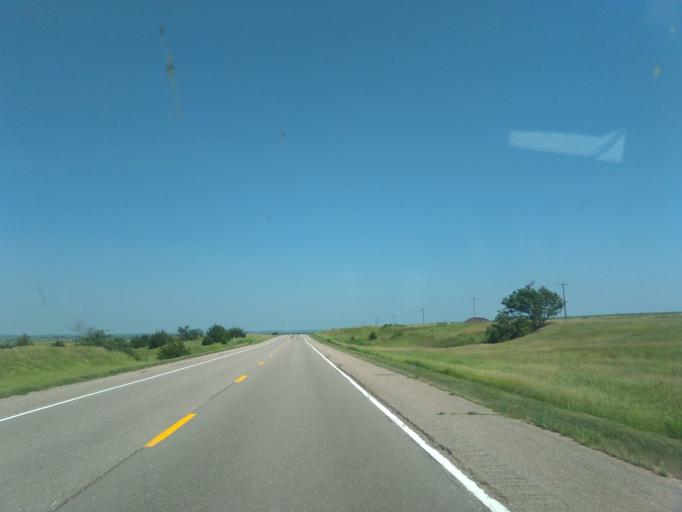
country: US
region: Nebraska
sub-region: Frontier County
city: Stockville
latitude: 40.6043
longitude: -100.6297
